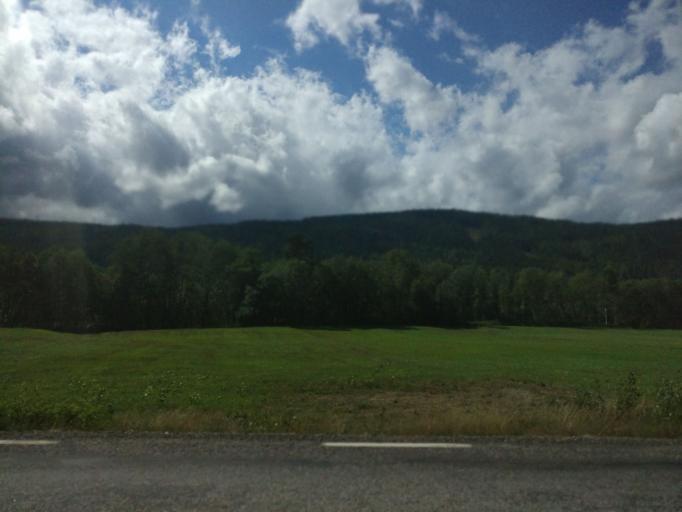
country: SE
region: Vaermland
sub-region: Hagfors Kommun
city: Ekshaerad
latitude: 60.3021
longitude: 13.3782
